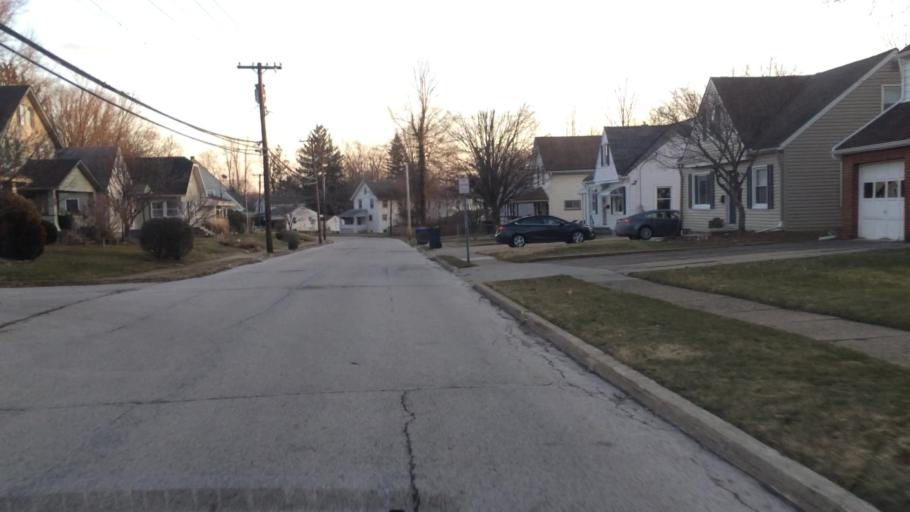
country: US
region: Ohio
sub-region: Summit County
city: Cuyahoga Falls
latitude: 41.1463
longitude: -81.4806
